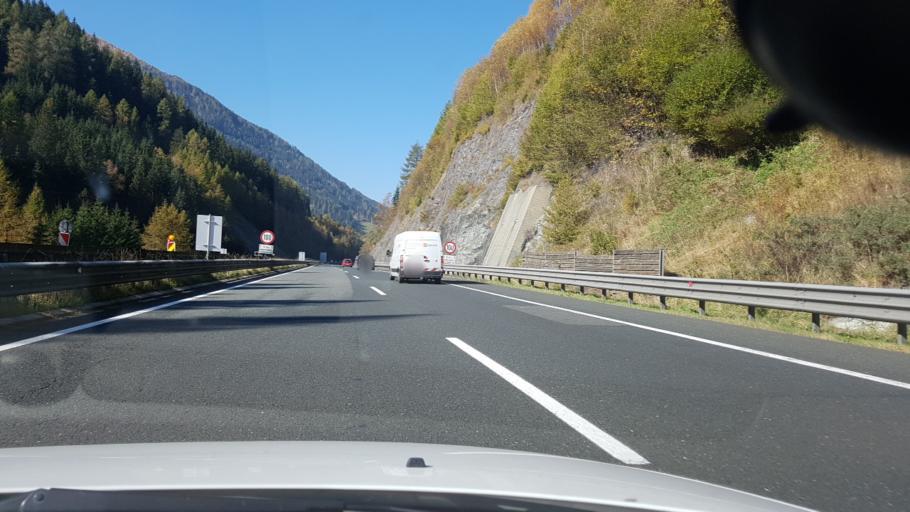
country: AT
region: Salzburg
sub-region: Politischer Bezirk Tamsweg
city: Zederhaus
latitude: 47.1377
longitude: 13.5377
